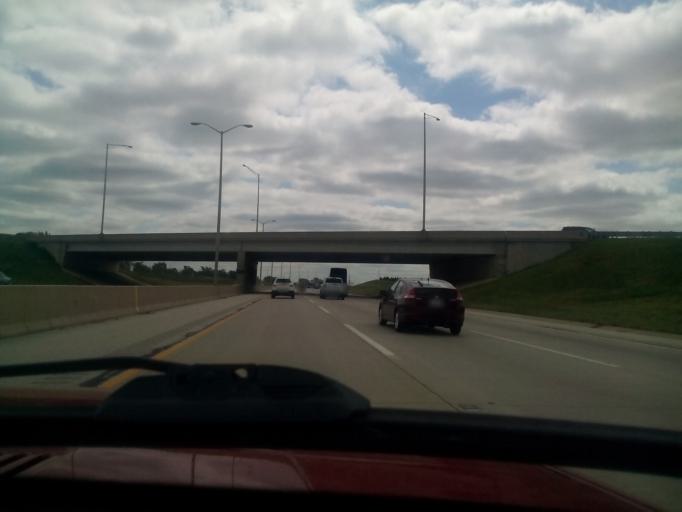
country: US
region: Illinois
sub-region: Cook County
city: Lemont
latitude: 41.6570
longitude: -88.0189
